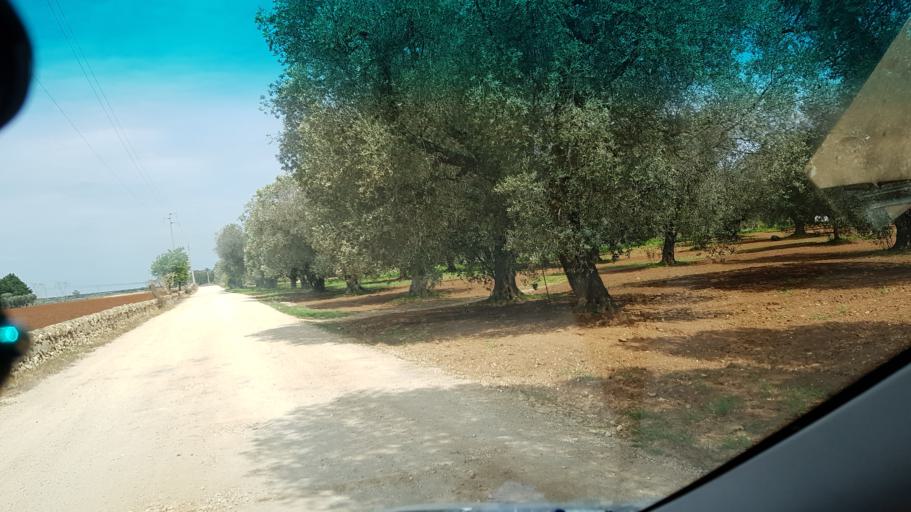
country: IT
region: Apulia
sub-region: Provincia di Brindisi
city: Mesagne
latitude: 40.6002
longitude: 17.8543
